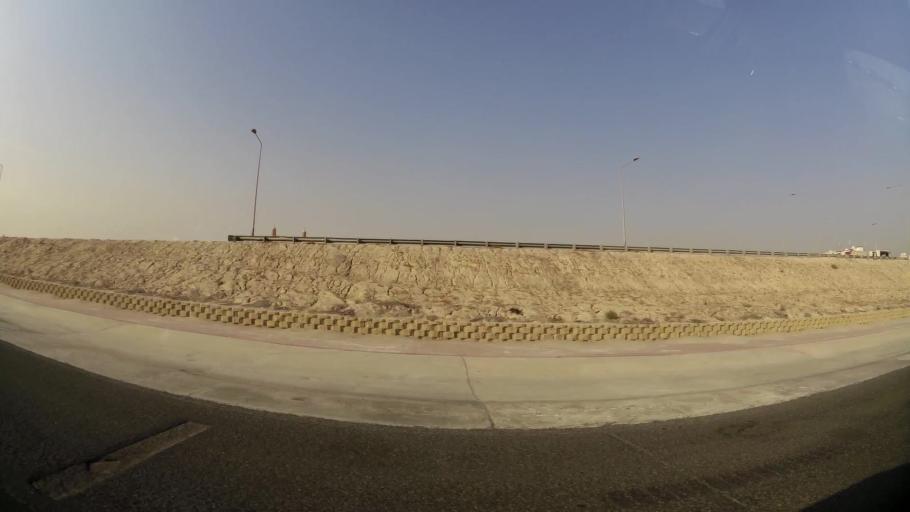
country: KW
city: Al Funaytis
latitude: 29.2478
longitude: 48.0919
